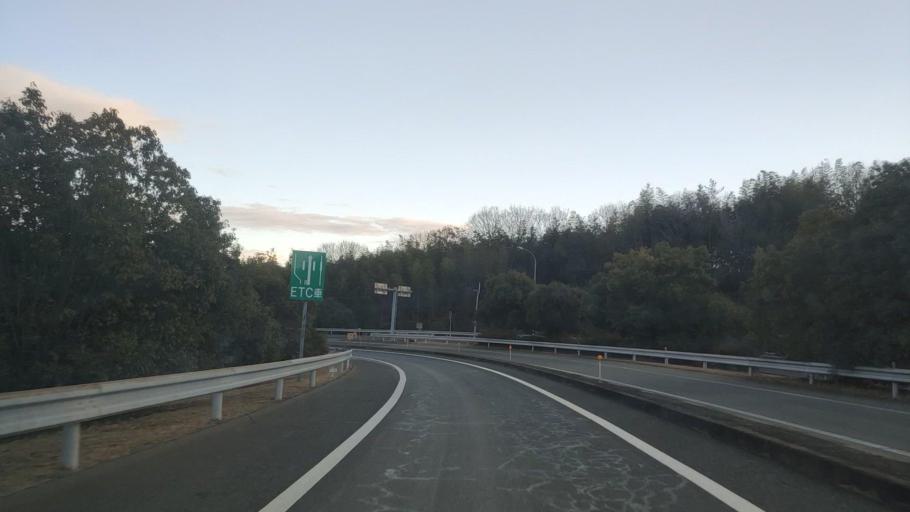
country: JP
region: Hyogo
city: Tatsunocho-tominaga
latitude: 34.8677
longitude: 134.6140
